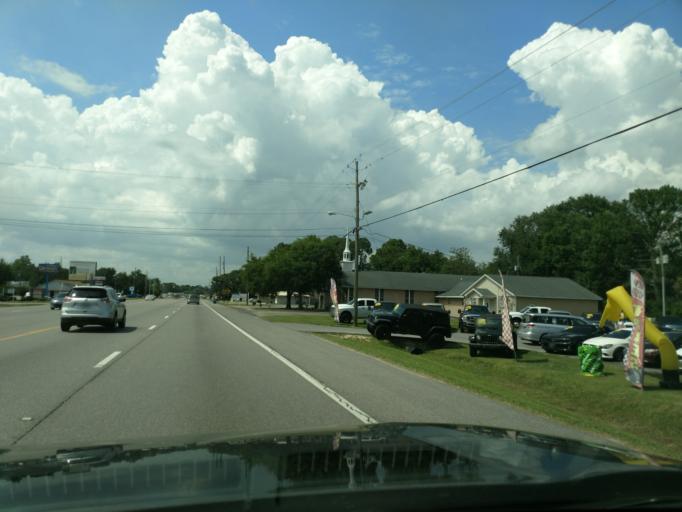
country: US
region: Mississippi
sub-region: Jackson County
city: Gulf Hills
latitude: 30.4297
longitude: -88.8293
